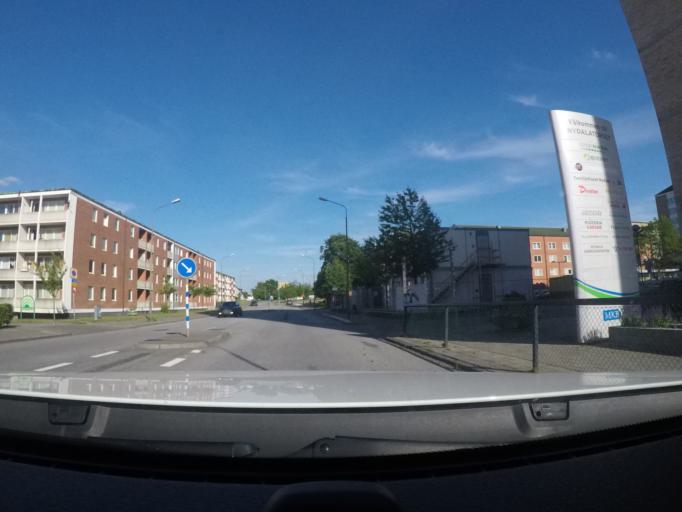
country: SE
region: Skane
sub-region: Malmo
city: Malmoe
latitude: 55.5741
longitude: 13.0212
